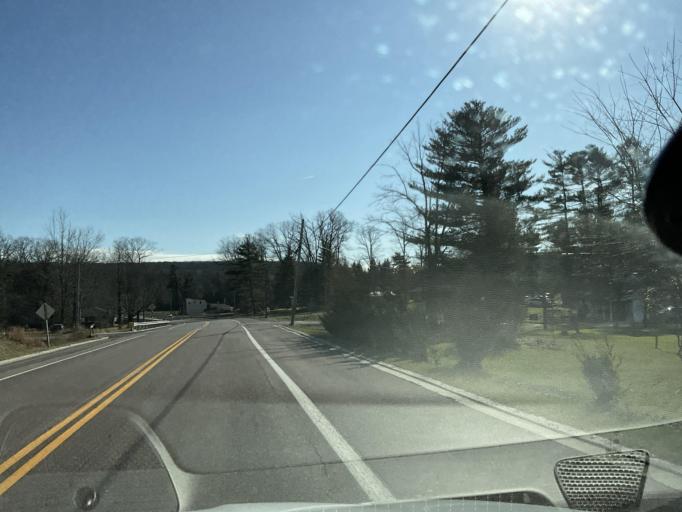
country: US
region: Maryland
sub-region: Garrett County
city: Oakland
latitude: 39.3928
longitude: -79.4652
